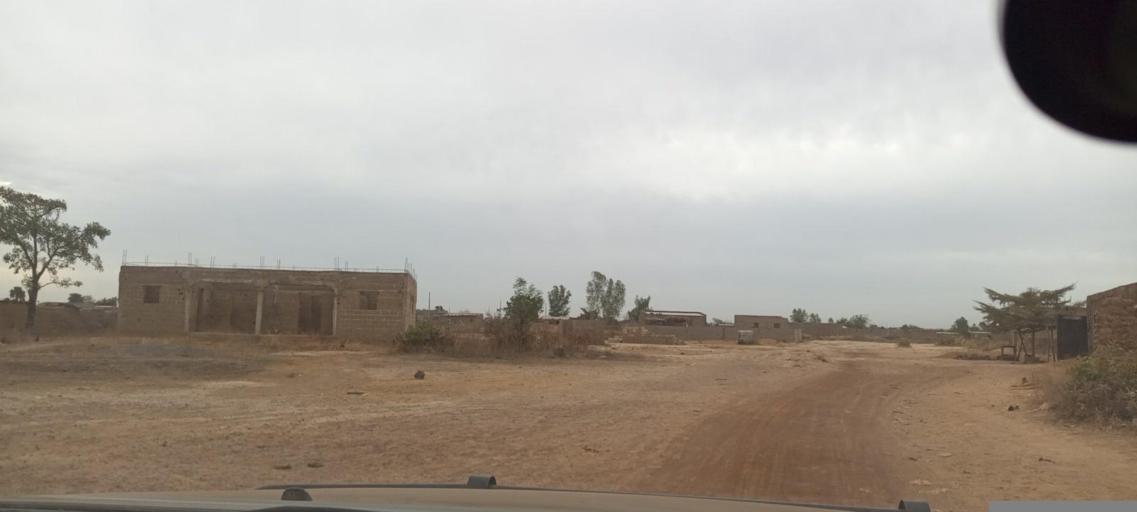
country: ML
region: Koulikoro
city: Kati
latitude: 12.7998
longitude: -8.2486
